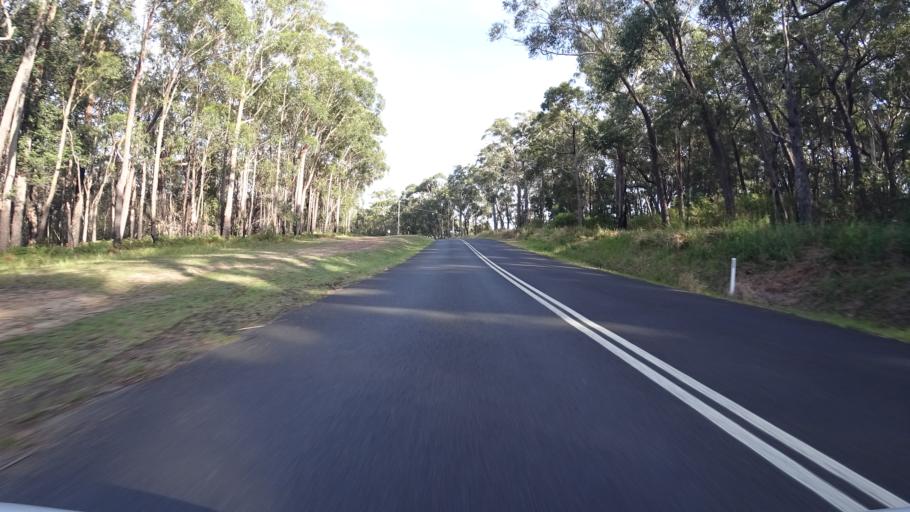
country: AU
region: New South Wales
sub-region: Shoalhaven Shire
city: Milton
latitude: -35.2614
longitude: 150.5069
